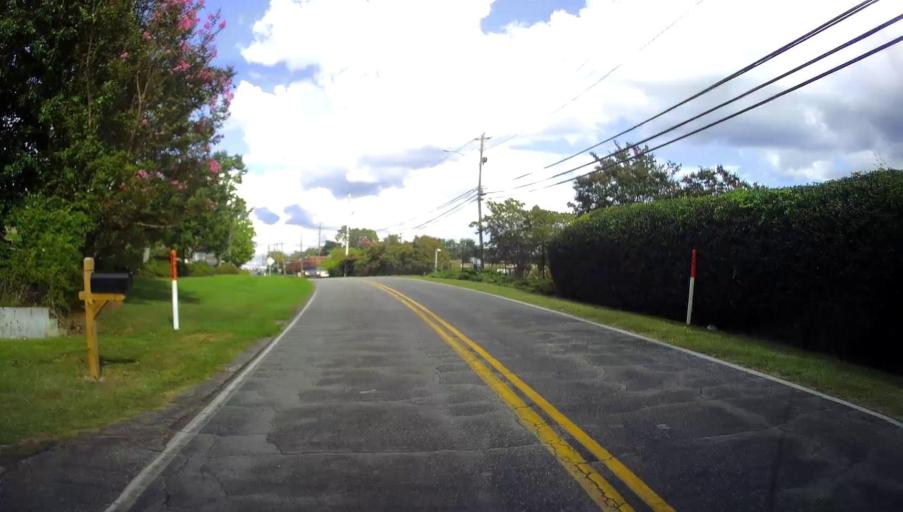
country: US
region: Alabama
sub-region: Russell County
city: Phenix City
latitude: 32.5208
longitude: -84.9686
